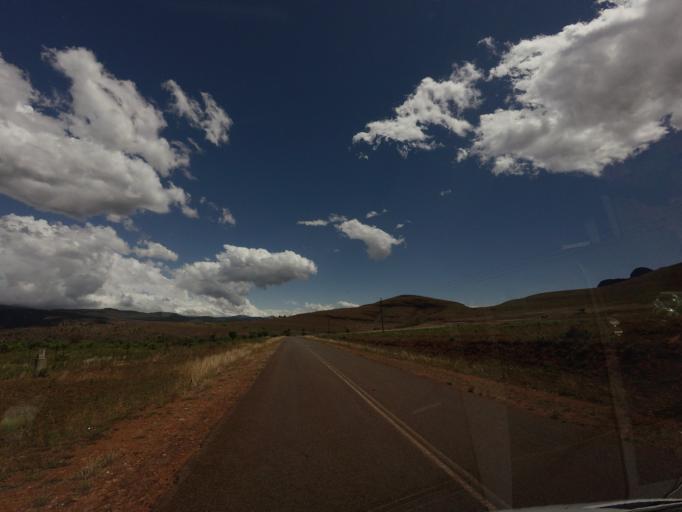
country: ZA
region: Mpumalanga
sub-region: Ehlanzeni District
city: Graksop
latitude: -24.6291
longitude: 30.8113
